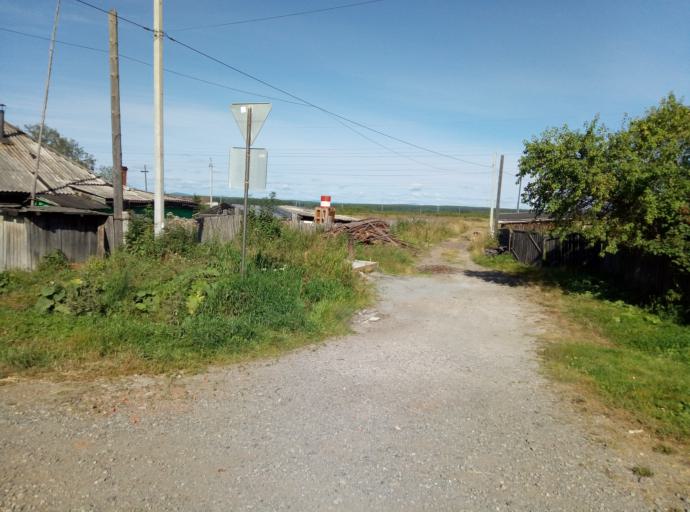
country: RU
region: Sverdlovsk
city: Karpinsk
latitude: 59.7849
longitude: 59.9891
